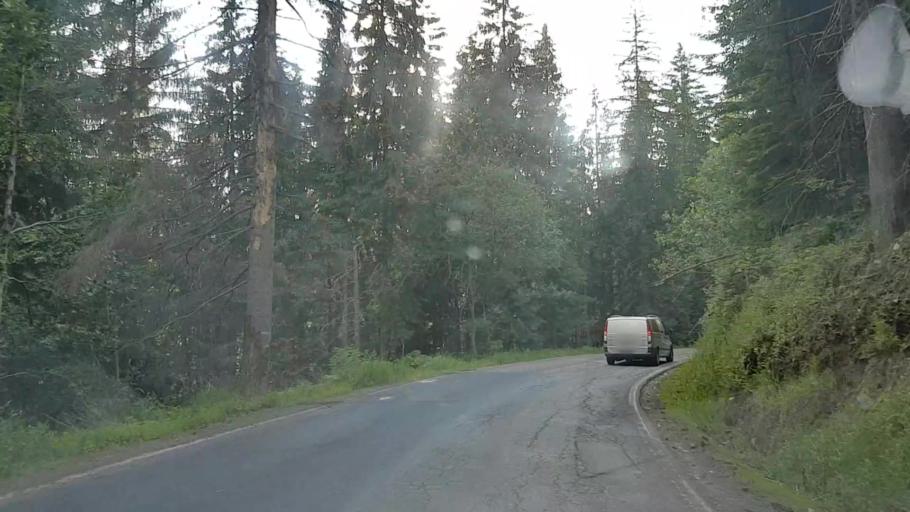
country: RO
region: Harghita
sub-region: Comuna Varsag
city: Varsag
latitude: 46.6631
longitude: 25.3160
